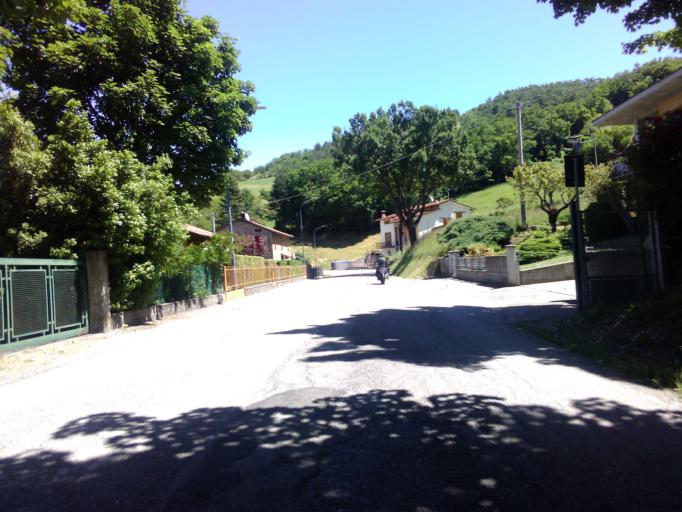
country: IT
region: Emilia-Romagna
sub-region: Provincia di Parma
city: Terenzo
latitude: 44.5774
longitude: 10.0778
